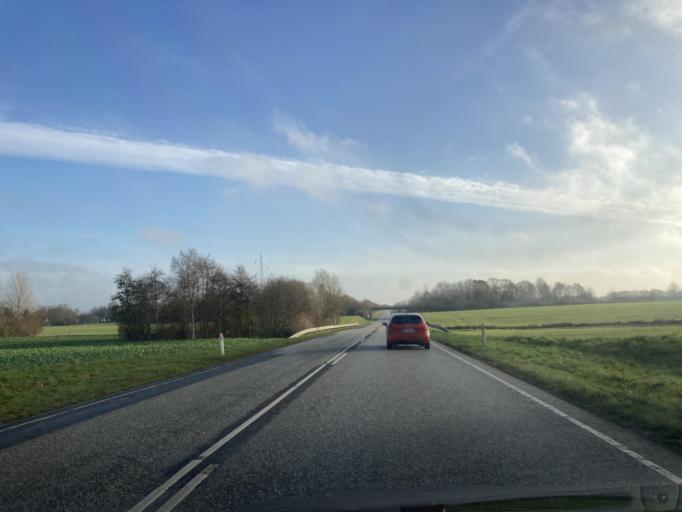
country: DK
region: Zealand
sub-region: Guldborgsund Kommune
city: Nykobing Falster
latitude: 54.7612
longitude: 11.7772
